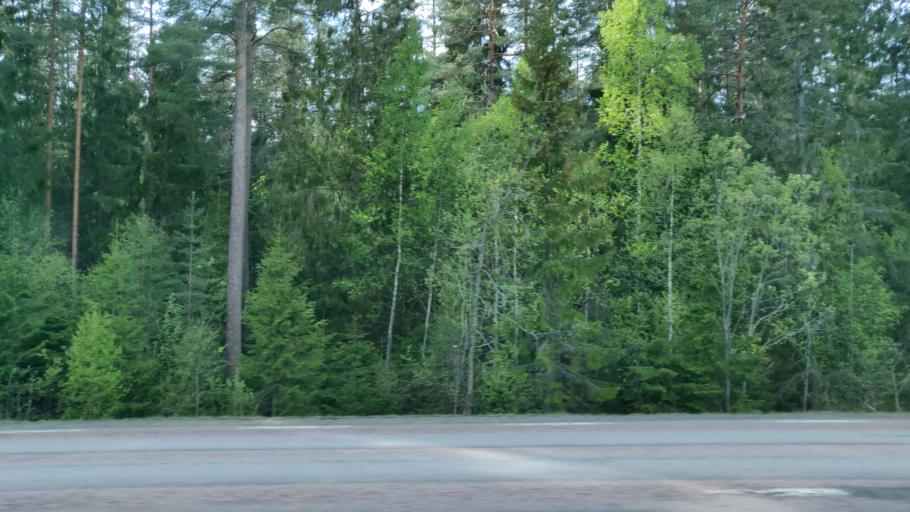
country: SE
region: Vaermland
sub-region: Forshaga Kommun
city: Forshaga
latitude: 59.5457
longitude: 13.4694
